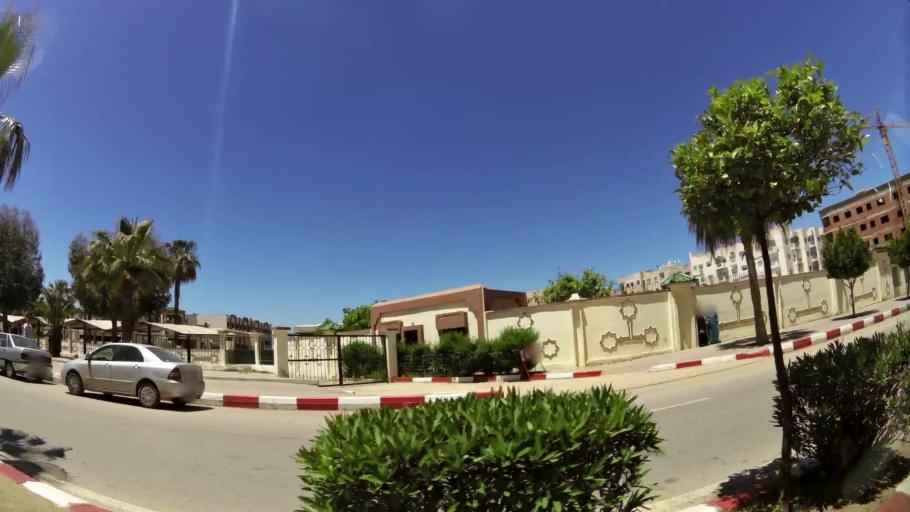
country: MA
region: Meknes-Tafilalet
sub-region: Meknes
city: Meknes
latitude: 33.8580
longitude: -5.5786
